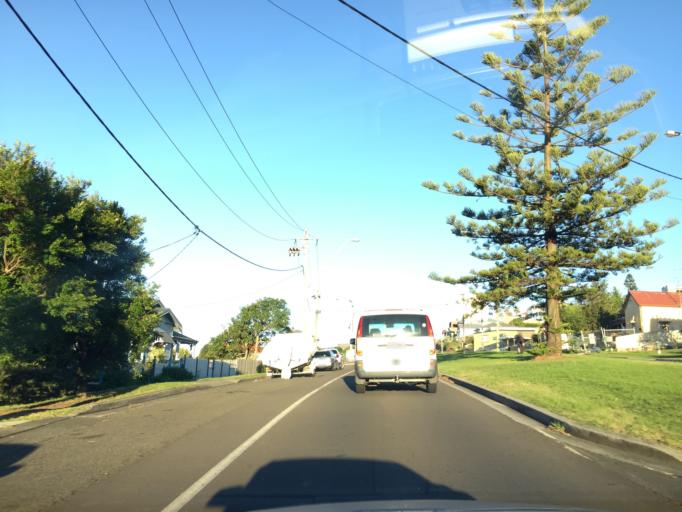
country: AU
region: New South Wales
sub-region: Kiama
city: Kiama
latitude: -34.6628
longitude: 150.8509
